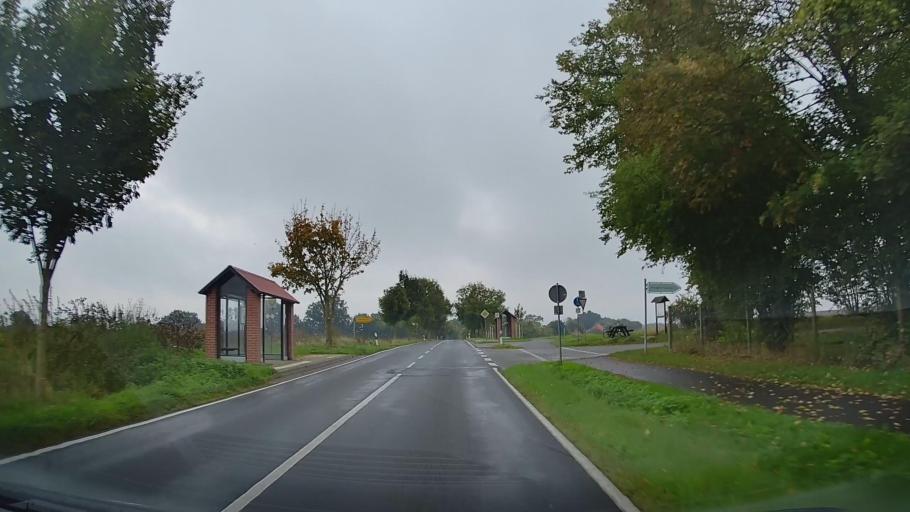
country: DE
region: Mecklenburg-Vorpommern
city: Ostseebad Boltenhagen
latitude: 53.9433
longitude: 11.2381
